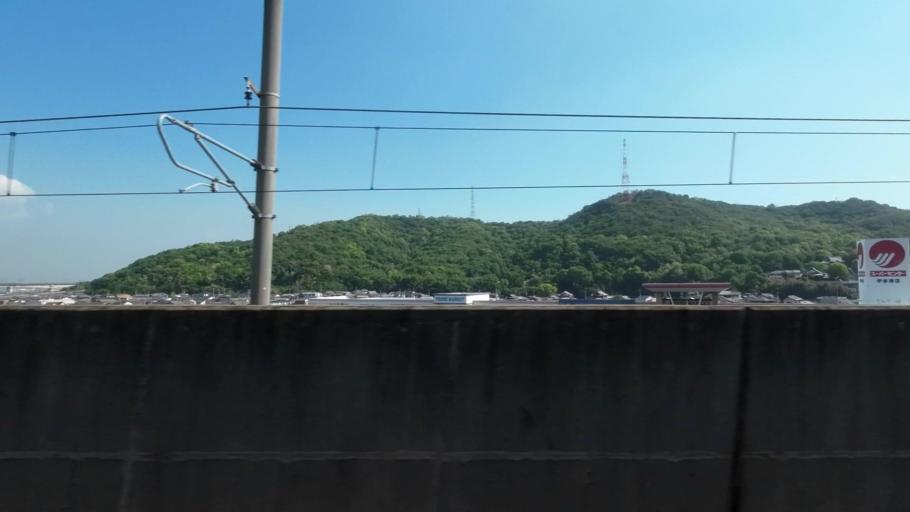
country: JP
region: Kagawa
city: Sakaidecho
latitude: 34.3125
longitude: 133.8295
